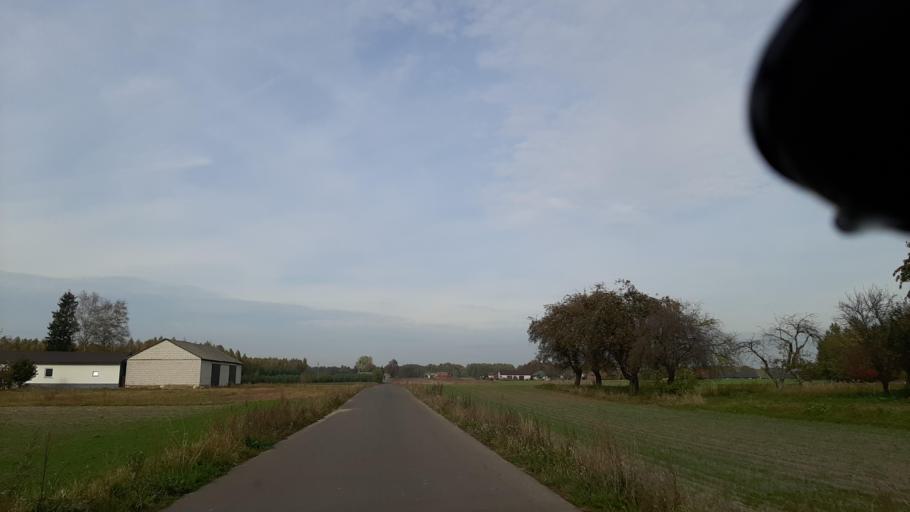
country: PL
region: Lublin Voivodeship
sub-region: Powiat lubelski
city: Garbow
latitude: 51.3969
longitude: 22.3248
